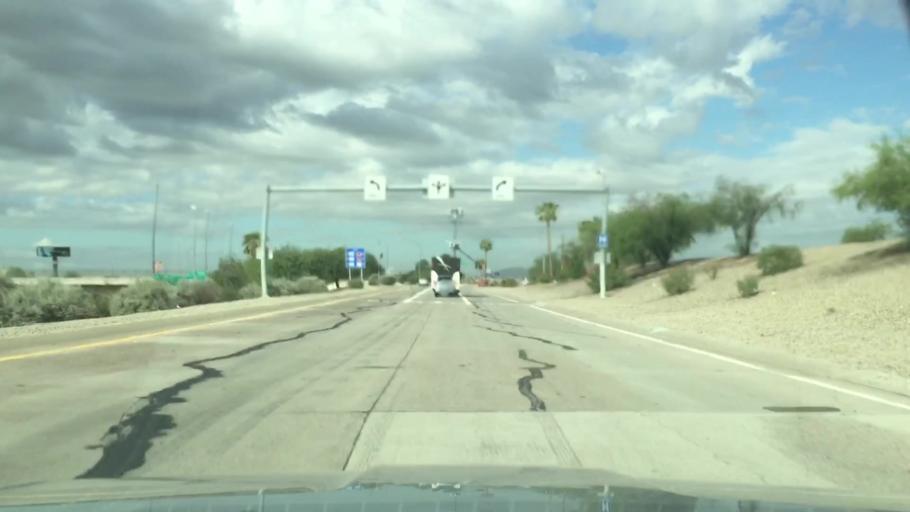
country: US
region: Arizona
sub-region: Maricopa County
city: Tolleson
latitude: 33.4629
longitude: -112.2532
